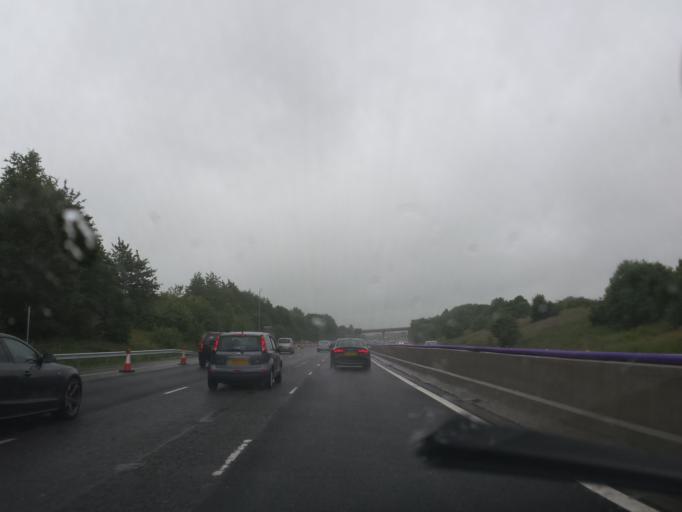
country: GB
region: England
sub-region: Derbyshire
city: Tibshelf
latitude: 53.1688
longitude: -1.3243
